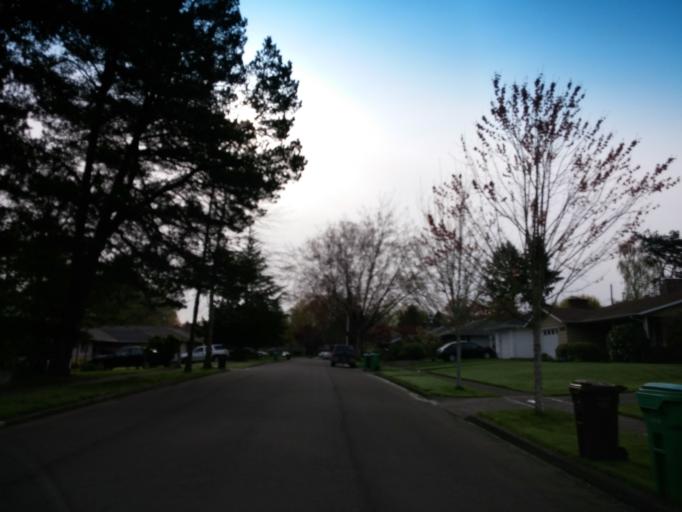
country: US
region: Oregon
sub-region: Washington County
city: Cedar Hills
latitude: 45.5102
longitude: -122.8051
